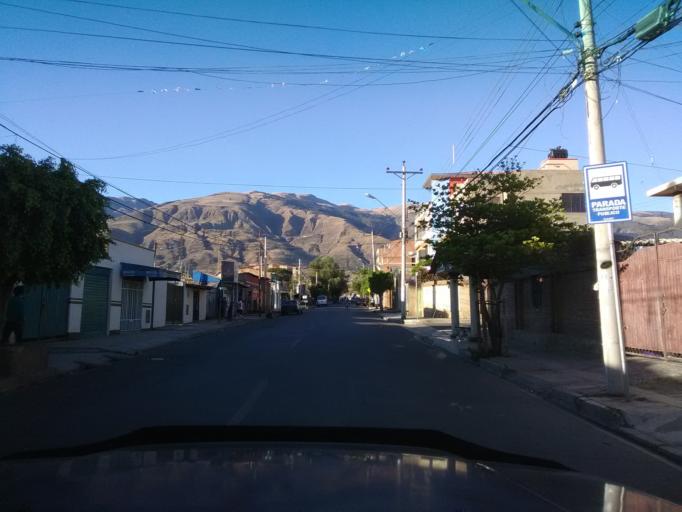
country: BO
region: Cochabamba
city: Cochabamba
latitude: -17.3612
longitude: -66.1847
